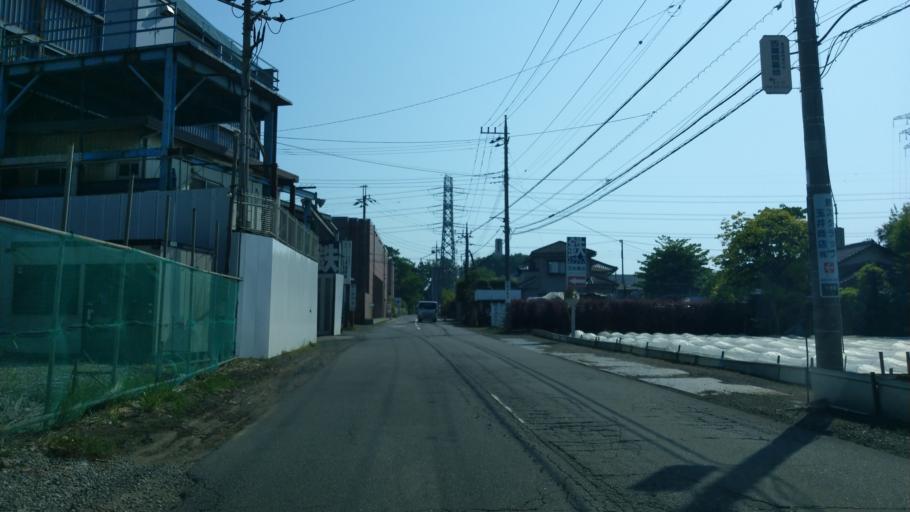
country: JP
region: Saitama
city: Oi
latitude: 35.8409
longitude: 139.4849
